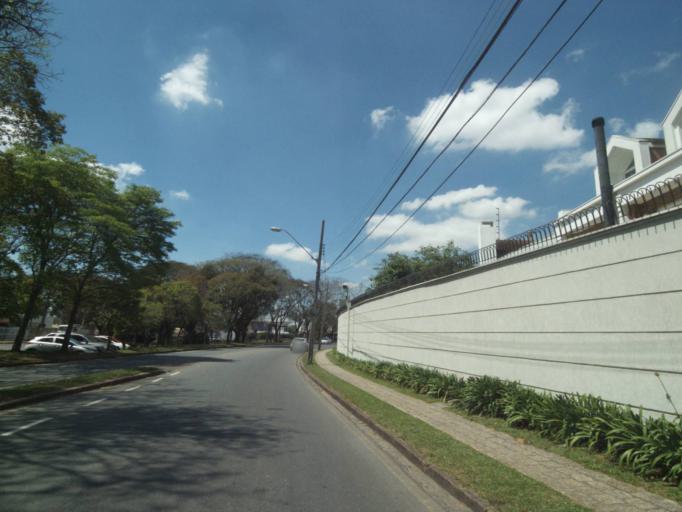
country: BR
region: Parana
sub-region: Curitiba
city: Curitiba
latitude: -25.4081
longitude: -49.2414
